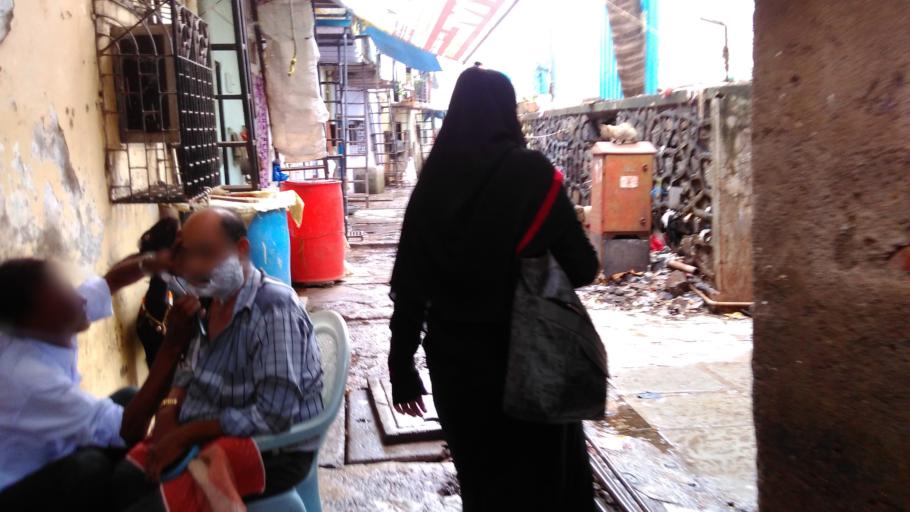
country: IN
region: Maharashtra
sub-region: Mumbai Suburban
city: Mumbai
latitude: 19.0625
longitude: 72.8794
